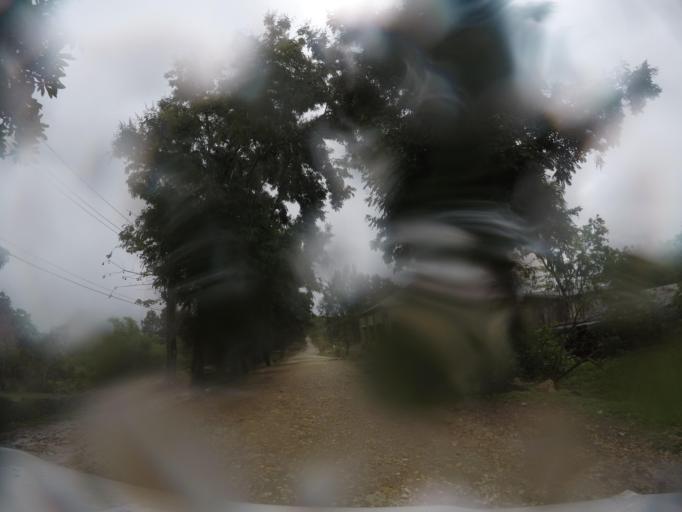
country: TL
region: Baucau
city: Venilale
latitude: -8.6438
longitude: 126.3774
